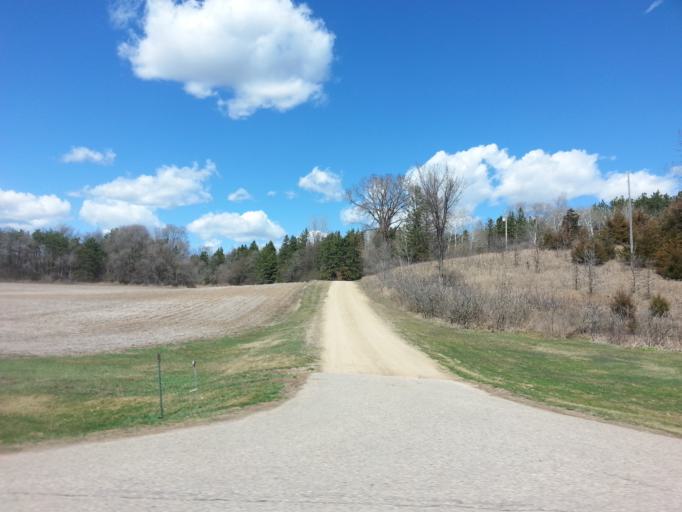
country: US
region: Minnesota
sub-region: Washington County
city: Cottage Grove
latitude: 44.7168
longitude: -92.9618
